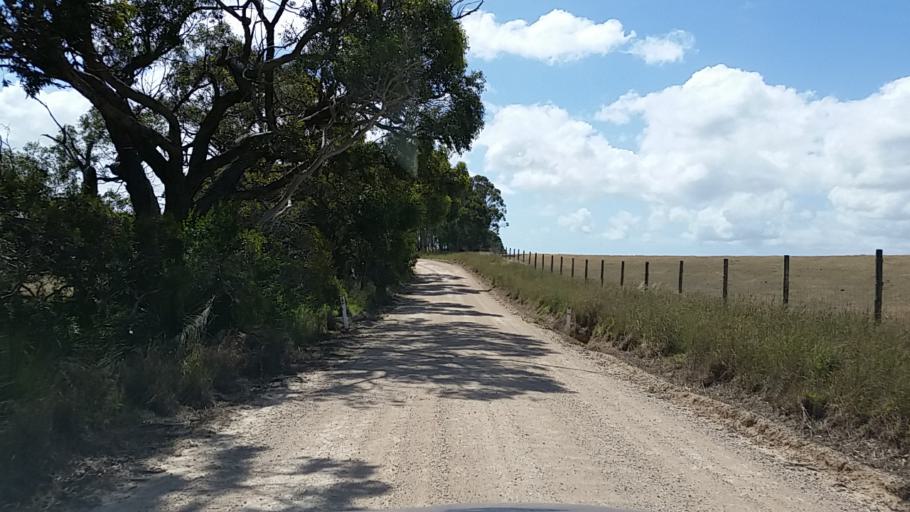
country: AU
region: South Australia
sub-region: Alexandrina
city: Port Elliot
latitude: -35.4499
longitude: 138.6510
